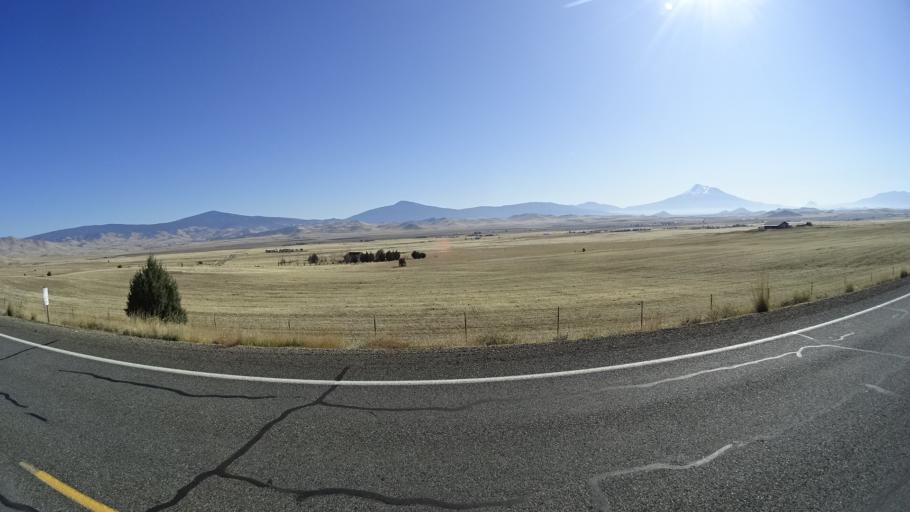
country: US
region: California
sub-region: Siskiyou County
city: Montague
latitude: 41.7971
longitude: -122.5109
